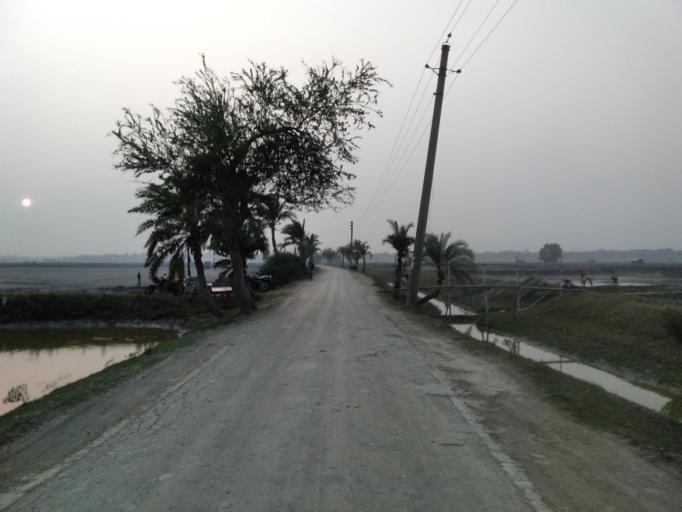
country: BD
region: Khulna
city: Satkhira
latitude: 22.6494
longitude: 89.0098
